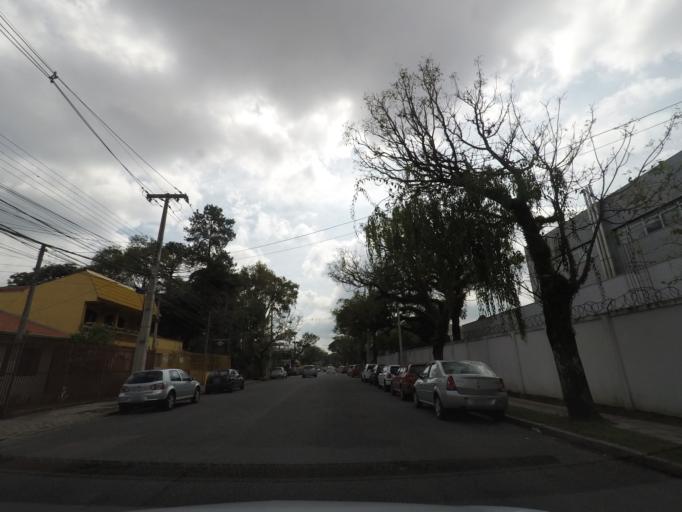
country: BR
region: Parana
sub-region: Curitiba
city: Curitiba
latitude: -25.4539
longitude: -49.2550
